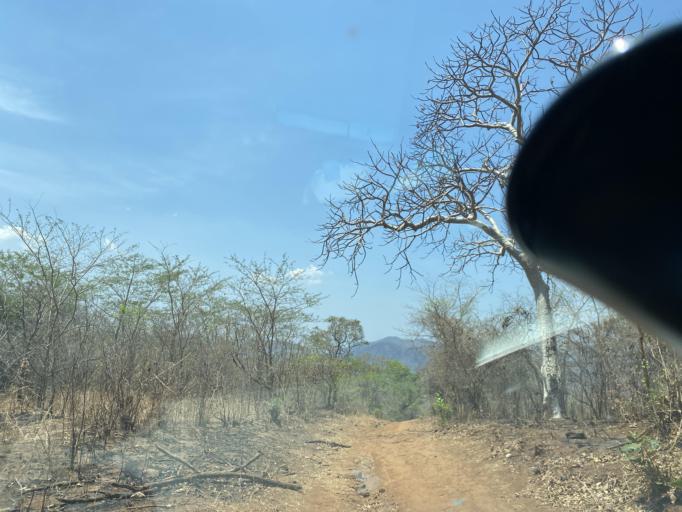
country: ZM
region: Lusaka
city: Kafue
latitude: -15.8008
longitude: 28.4519
